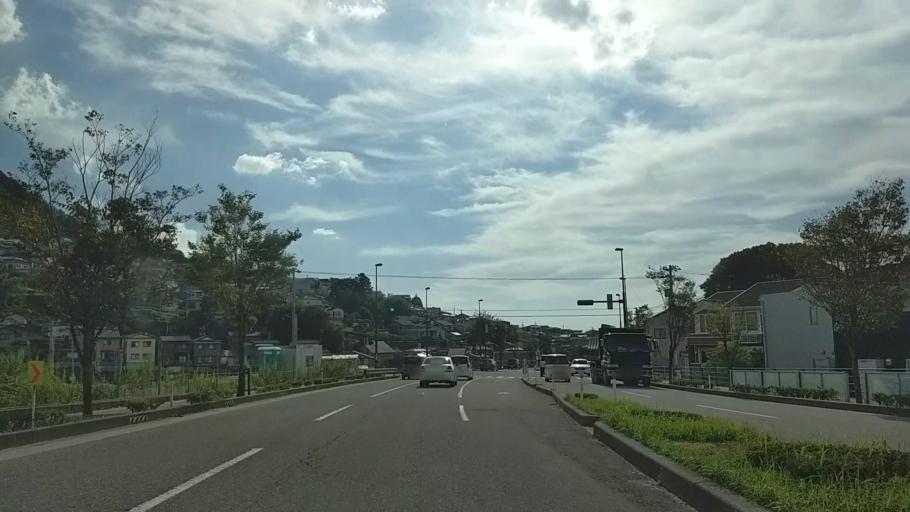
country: JP
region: Ishikawa
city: Nonoichi
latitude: 36.5283
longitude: 136.6513
